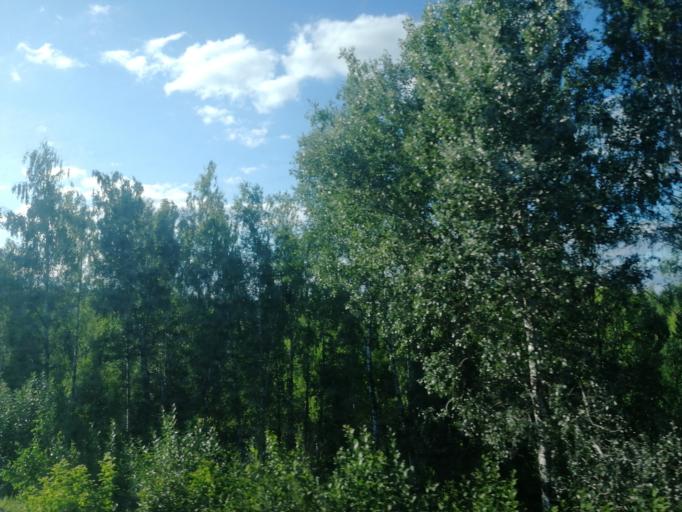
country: RU
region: Tula
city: Novogurovskiy
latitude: 54.2801
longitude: 37.2070
